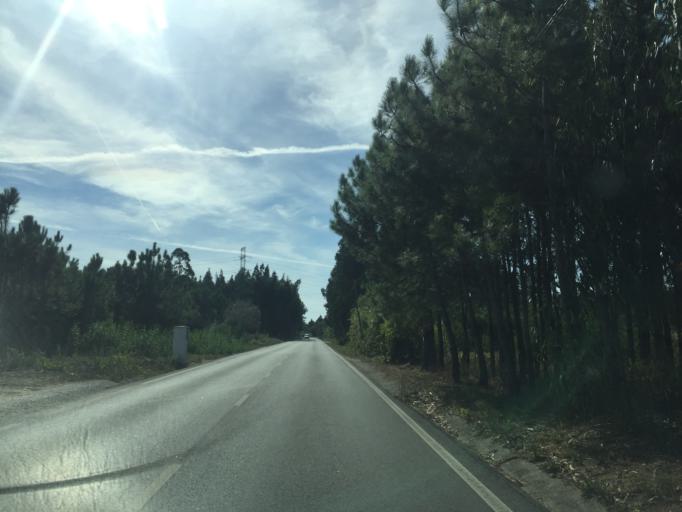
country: PT
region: Coimbra
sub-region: Figueira da Foz
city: Lavos
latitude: 40.0799
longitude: -8.8234
